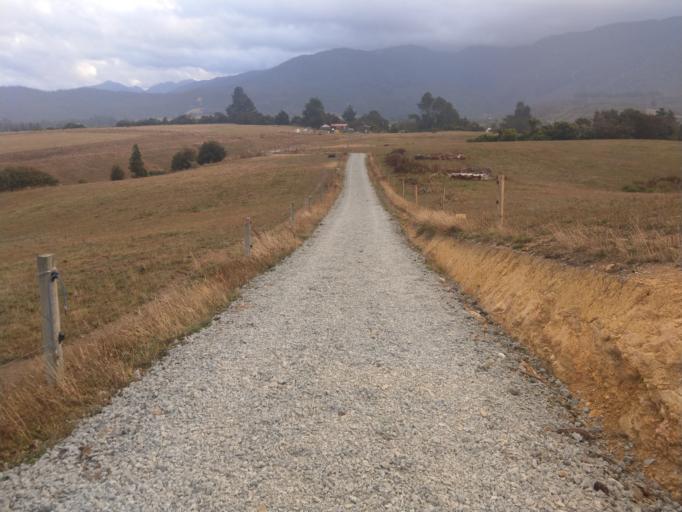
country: NZ
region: Tasman
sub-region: Tasman District
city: Takaka
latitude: -40.7904
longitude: 172.7446
